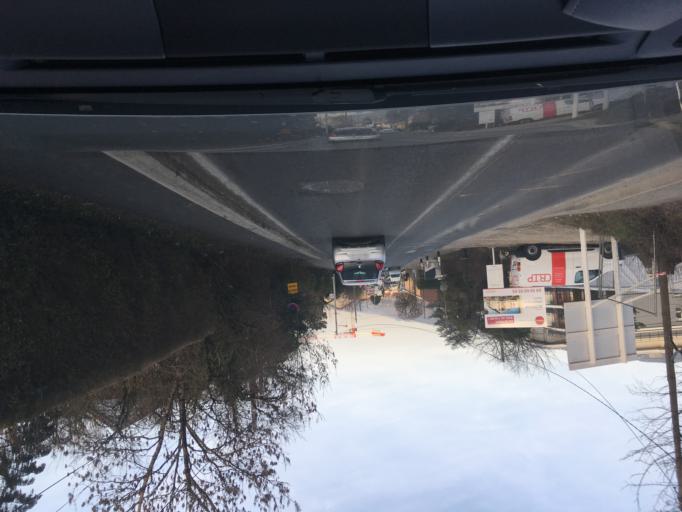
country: FR
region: Rhone-Alpes
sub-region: Departement de la Haute-Savoie
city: Vetraz-Monthoux
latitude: 46.1890
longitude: 6.2642
